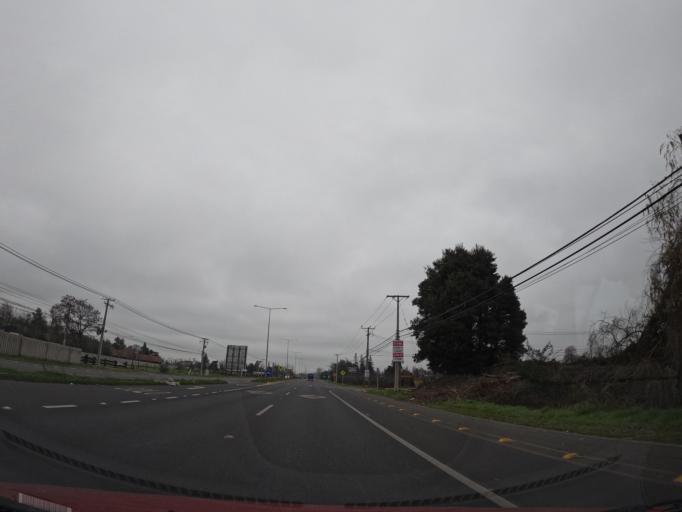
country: CL
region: Maule
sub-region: Provincia de Talca
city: Talca
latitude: -35.4492
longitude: -71.5990
